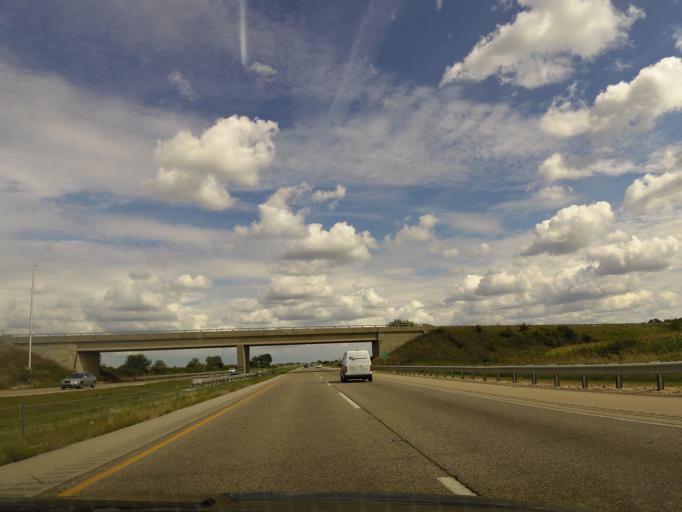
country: US
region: Illinois
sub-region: Kane County
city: Maple Park
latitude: 41.8645
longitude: -88.5628
